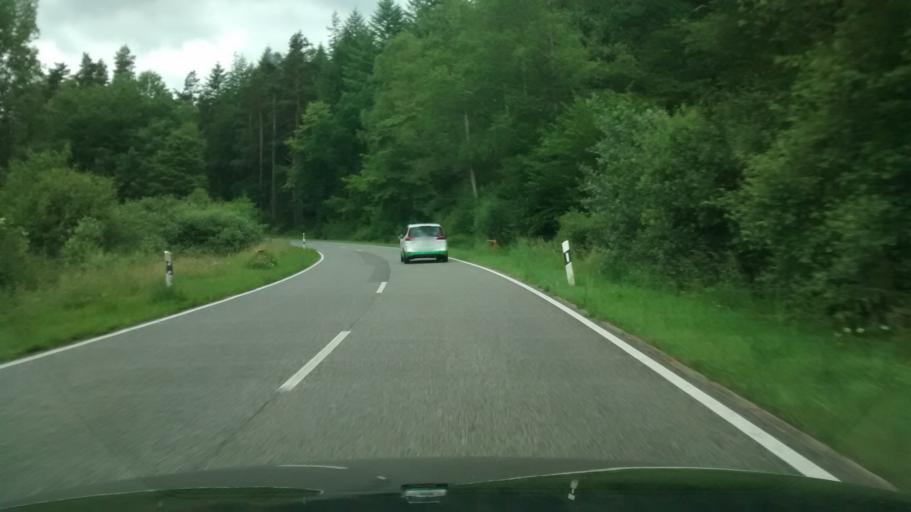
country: DE
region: Rheinland-Pfalz
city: Vorderweidenthal
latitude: 49.1157
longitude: 7.8955
